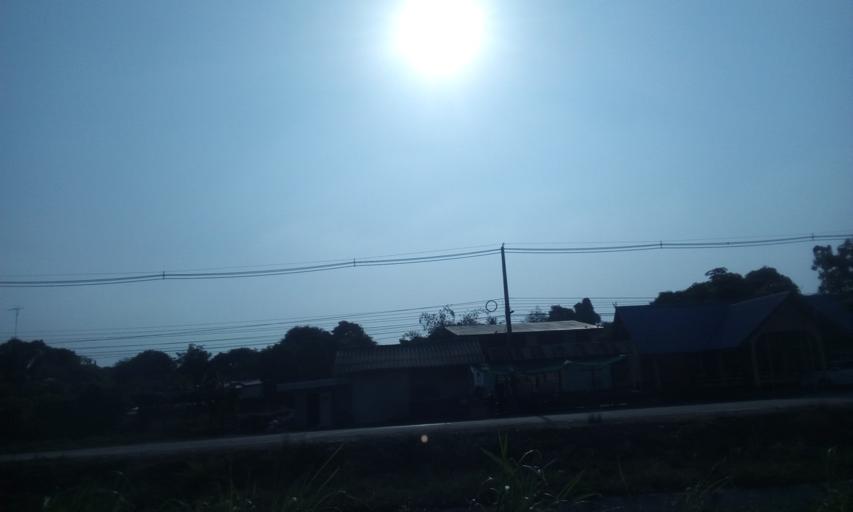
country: TH
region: Sing Buri
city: Sing Buri
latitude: 14.8520
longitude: 100.4135
